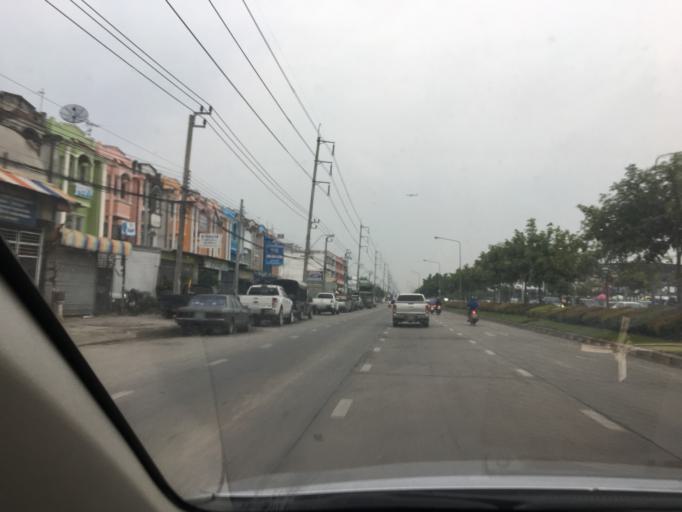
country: TH
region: Bangkok
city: Lat Krabang
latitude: 13.7529
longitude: 100.7734
